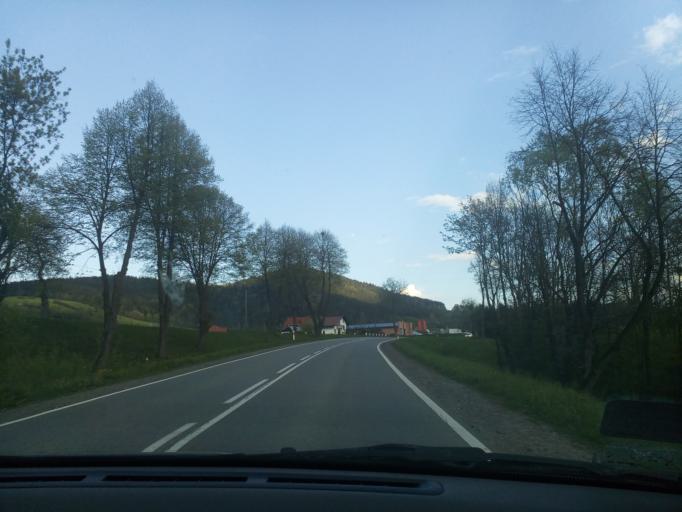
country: PL
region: Lesser Poland Voivodeship
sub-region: Powiat nowosadecki
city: Labowa
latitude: 49.5263
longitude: 20.8667
